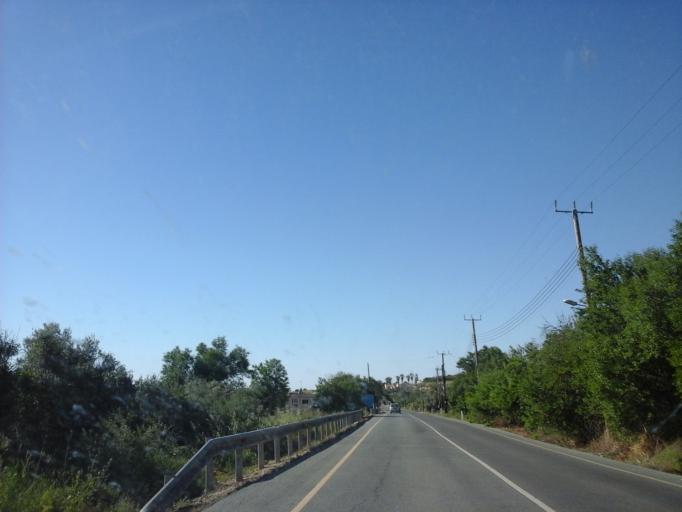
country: CY
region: Pafos
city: Polis
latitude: 34.9928
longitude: 32.4493
